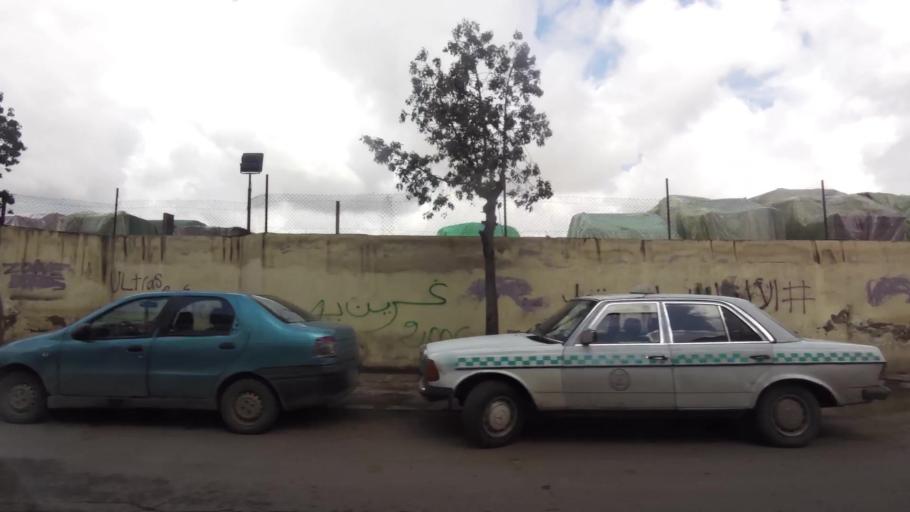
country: MA
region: Grand Casablanca
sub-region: Nouaceur
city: Bouskoura
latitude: 33.5167
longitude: -7.6542
